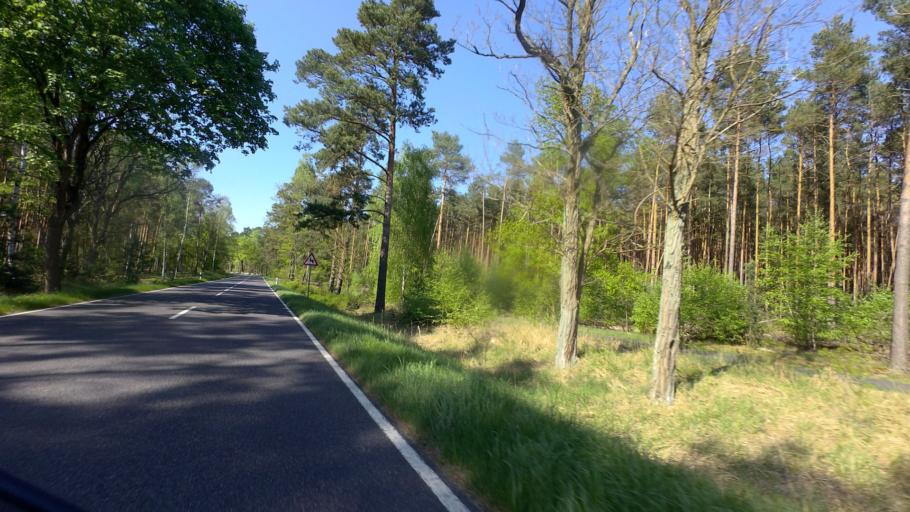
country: DE
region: Brandenburg
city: Halbe
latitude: 52.1487
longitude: 13.7452
